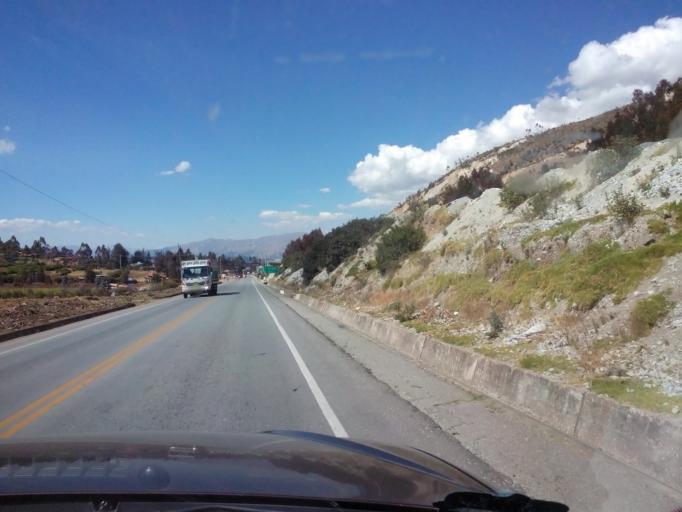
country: PE
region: Cusco
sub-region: Provincia de Anta
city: Ancahuasi
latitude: -13.4411
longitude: -72.3551
